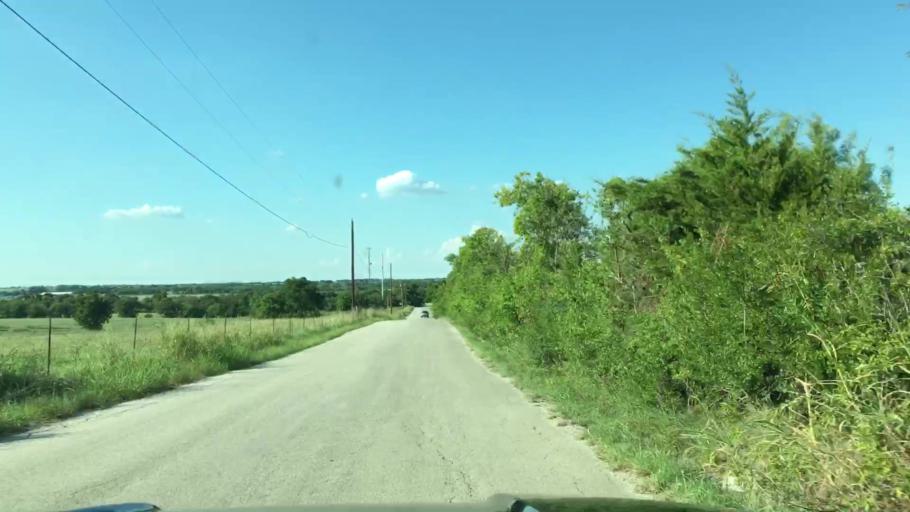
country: US
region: Texas
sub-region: Tarrant County
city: Haslet
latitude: 33.0253
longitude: -97.3766
